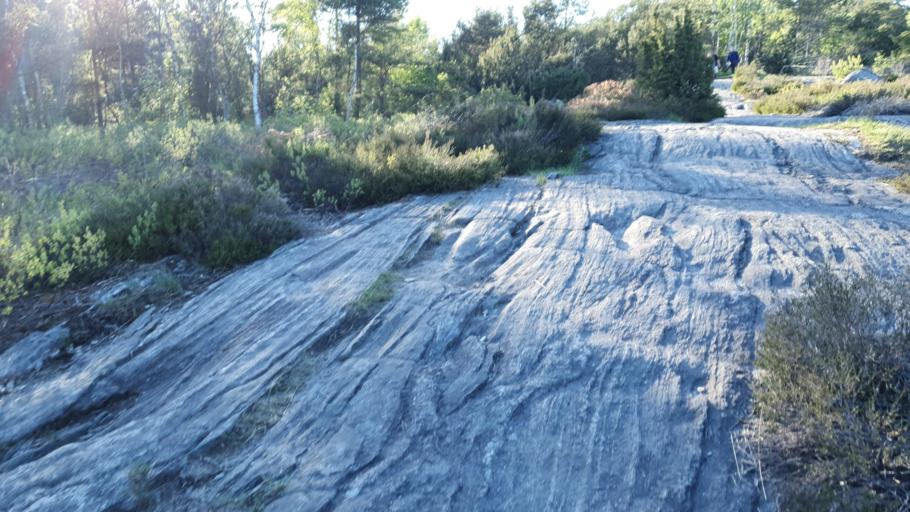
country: SE
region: Vaestra Goetaland
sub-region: Molndal
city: Kallered
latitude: 57.6291
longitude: 12.0642
